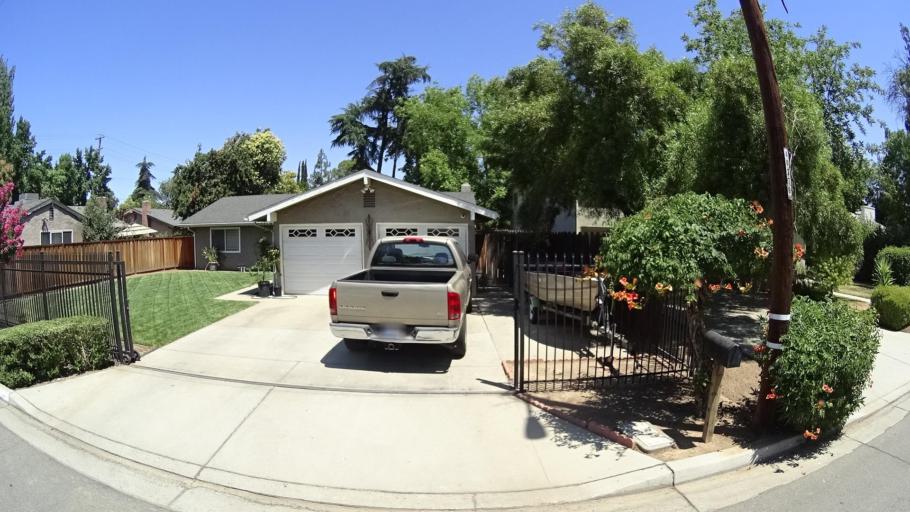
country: US
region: California
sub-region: Fresno County
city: Fresno
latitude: 36.7913
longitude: -119.7989
